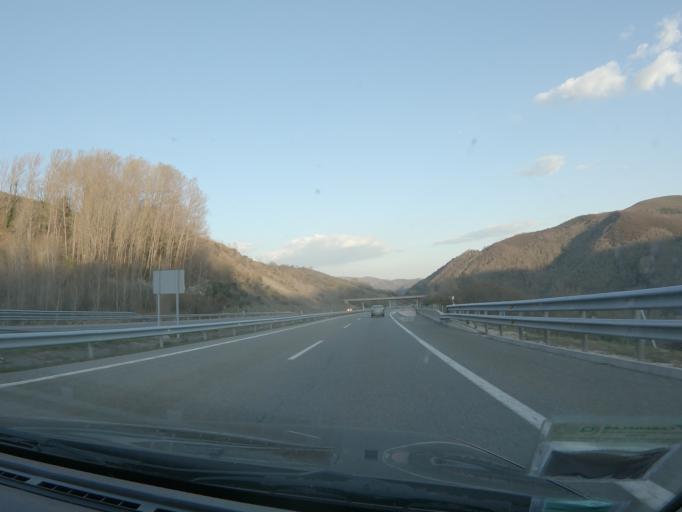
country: ES
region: Castille and Leon
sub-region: Provincia de Leon
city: Vega de Valcarce
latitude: 42.6690
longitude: -6.9494
